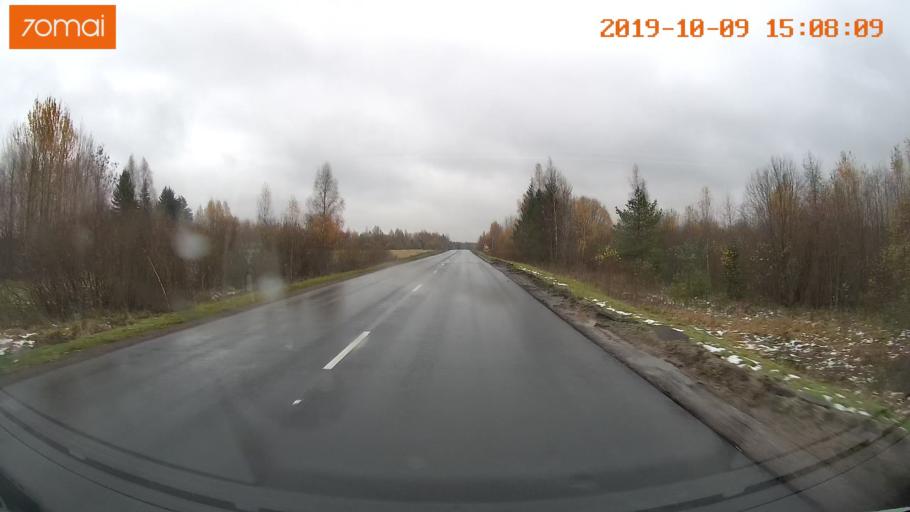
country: RU
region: Kostroma
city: Susanino
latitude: 58.2101
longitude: 41.6480
